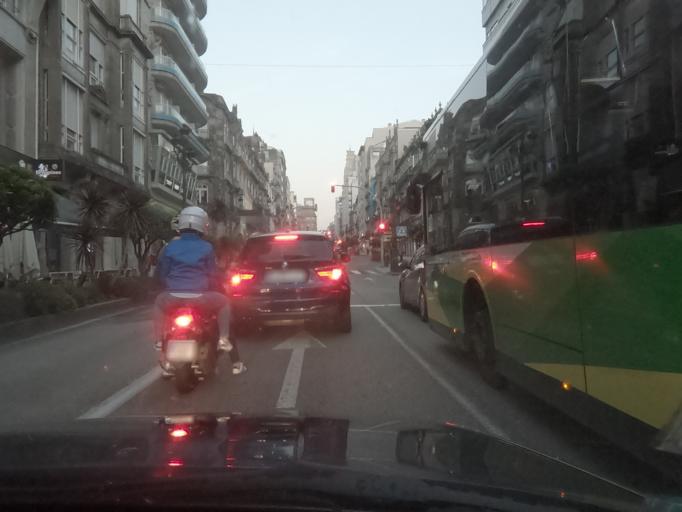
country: ES
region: Galicia
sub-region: Provincia de Pontevedra
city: Vigo
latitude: 42.2361
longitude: -8.7195
